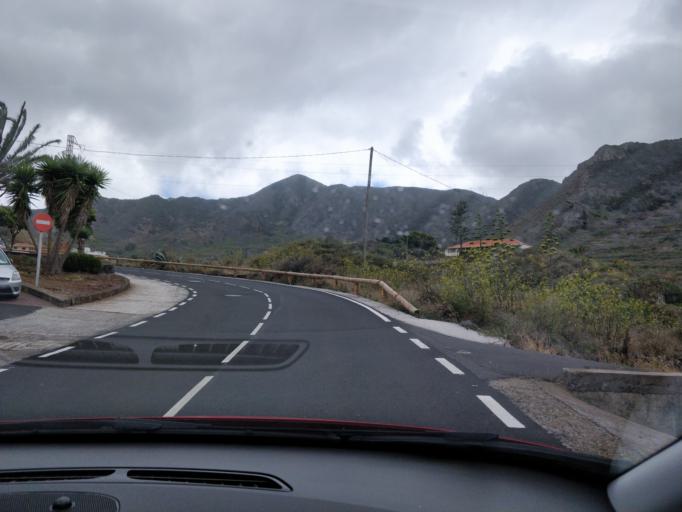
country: ES
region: Canary Islands
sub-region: Provincia de Santa Cruz de Tenerife
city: Tanque
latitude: 28.3460
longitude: -16.8461
